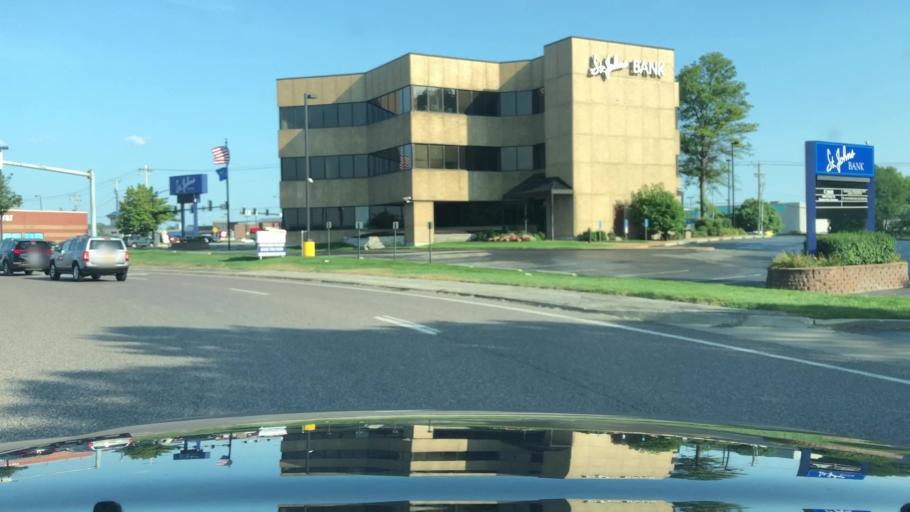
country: US
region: Missouri
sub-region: Saint Charles County
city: Saint Peters
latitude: 38.7920
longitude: -90.5669
